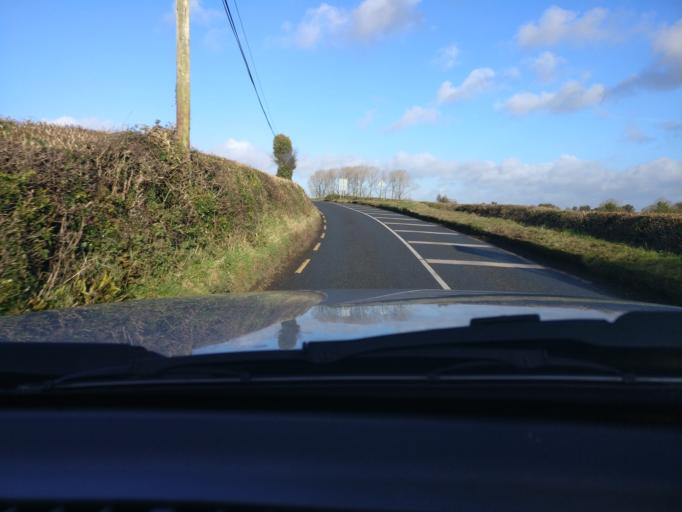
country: IE
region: Leinster
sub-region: Uibh Fhaili
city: Clara
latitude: 53.4002
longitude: -7.5789
